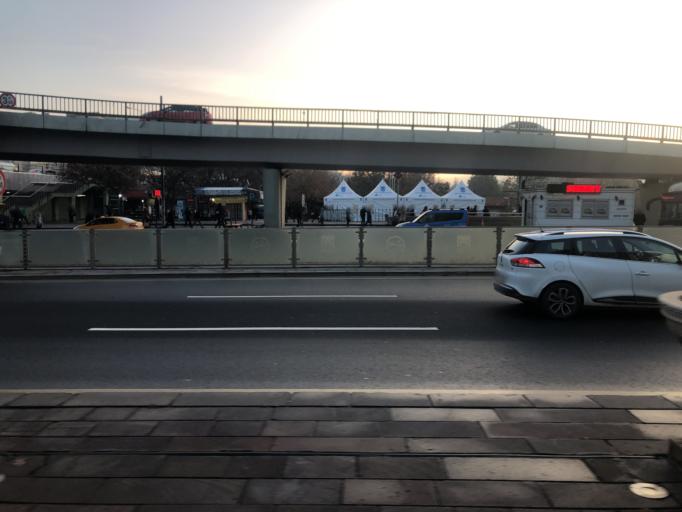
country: TR
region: Ankara
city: Ankara
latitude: 39.9287
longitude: 32.8548
